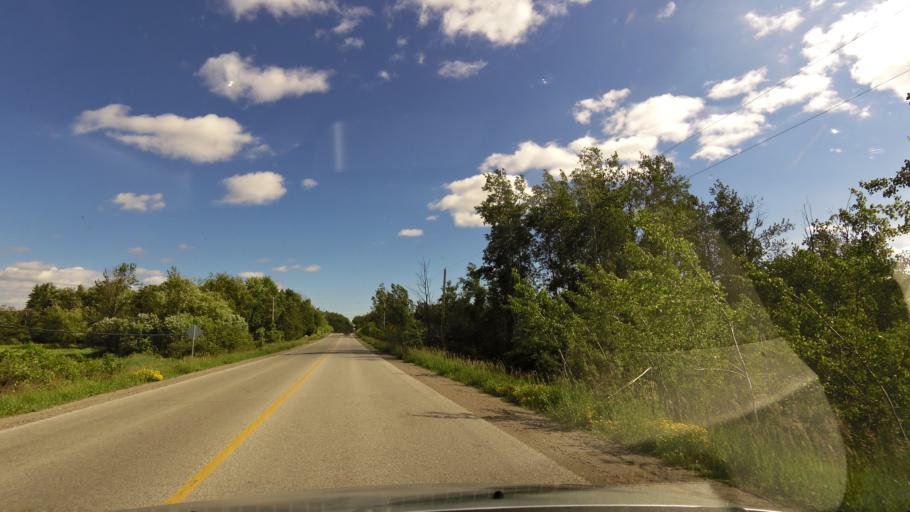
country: CA
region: Ontario
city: Bradford West Gwillimbury
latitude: 44.1777
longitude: -79.6194
